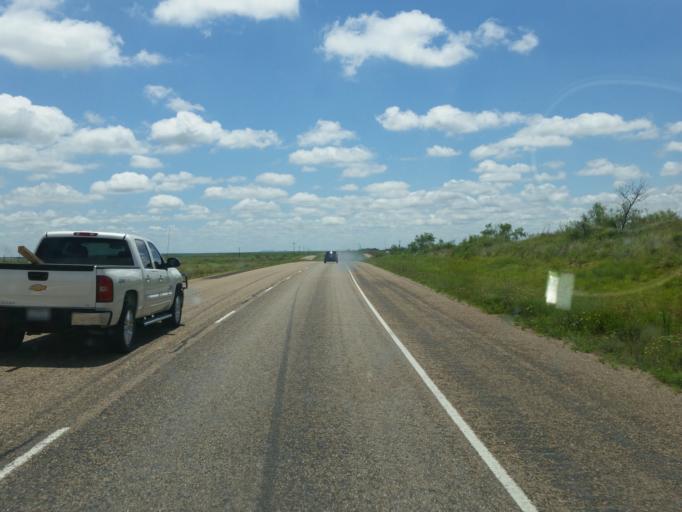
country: US
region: Texas
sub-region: Garza County
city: Post
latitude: 33.1383
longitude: -101.3133
